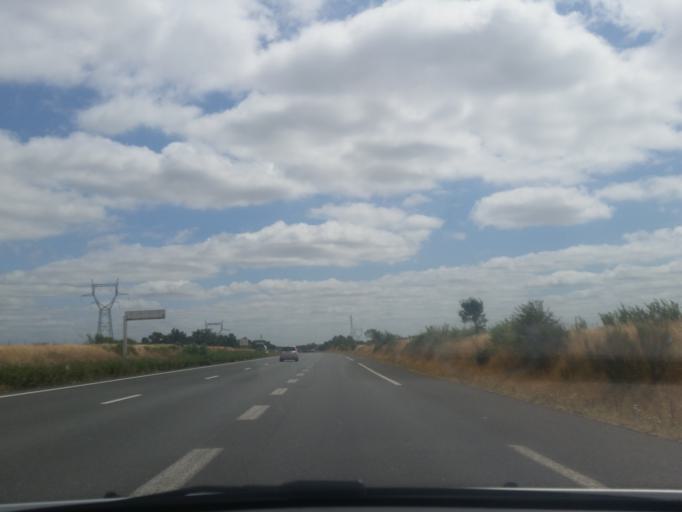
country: FR
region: Pays de la Loire
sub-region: Departement de la Loire-Atlantique
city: Varades
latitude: 47.4184
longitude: -1.0116
